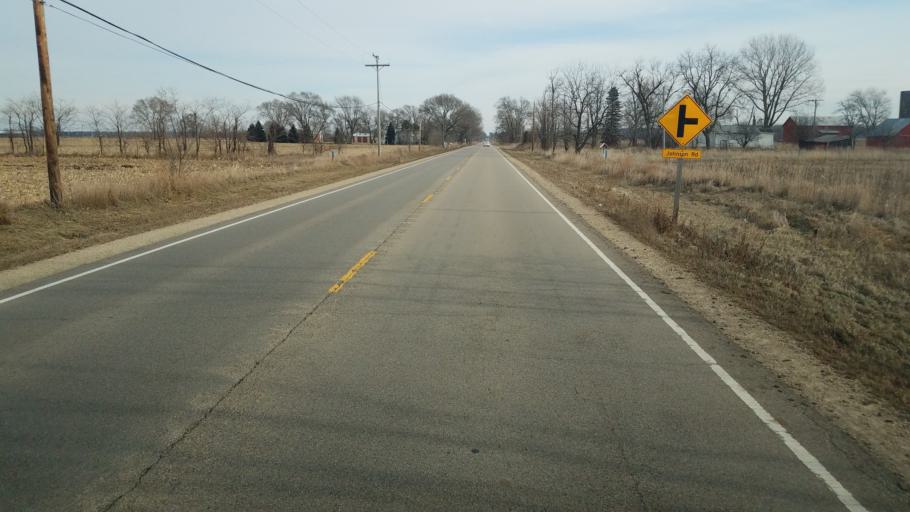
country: US
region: Illinois
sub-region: McHenry County
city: Marengo
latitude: 42.2504
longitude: -88.6550
